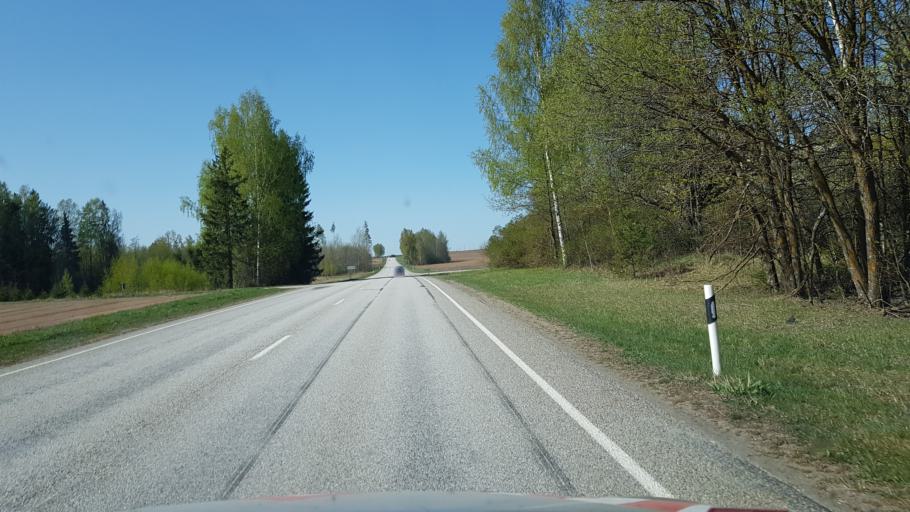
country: EE
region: Valgamaa
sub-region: Torva linn
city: Torva
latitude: 57.9339
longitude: 25.9987
